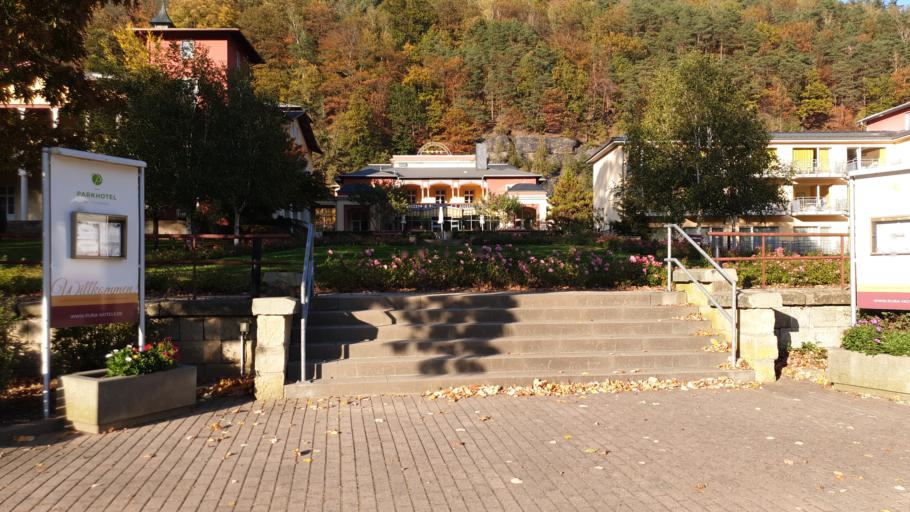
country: DE
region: Saxony
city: Bad Schandau
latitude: 50.9152
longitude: 14.1613
